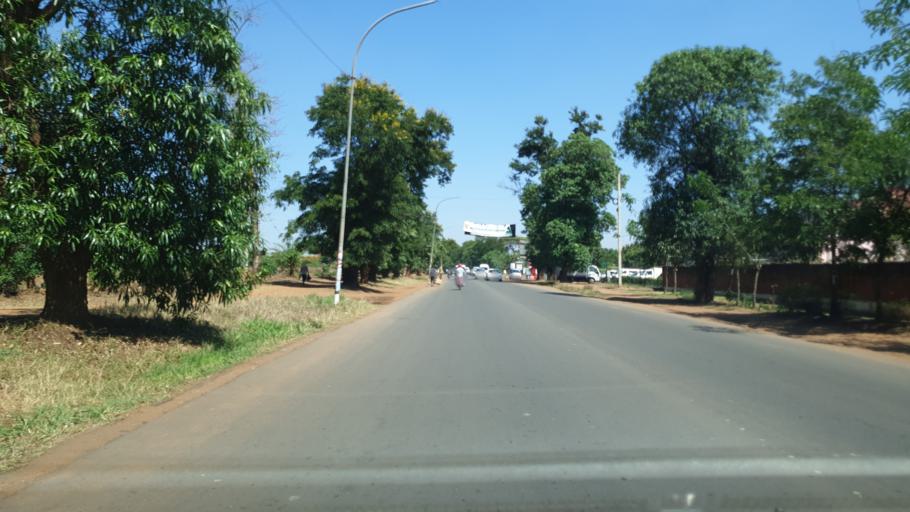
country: MW
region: Central Region
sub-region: Lilongwe District
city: Lilongwe
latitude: -13.9793
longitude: 33.7616
